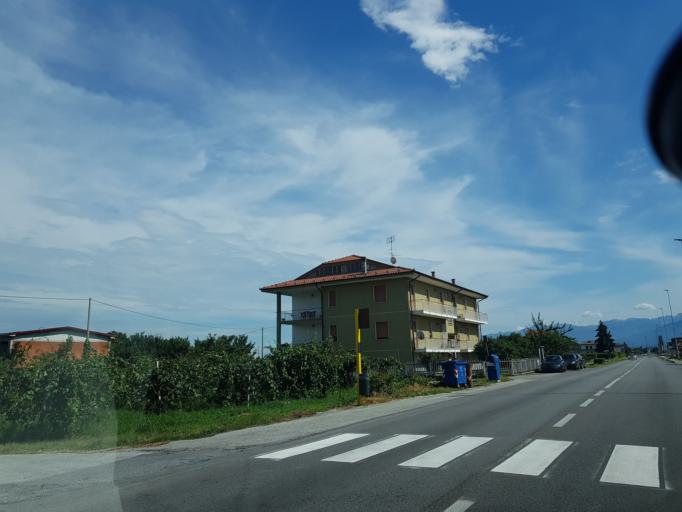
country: IT
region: Piedmont
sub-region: Provincia di Cuneo
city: Roata Rossi
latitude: 44.4770
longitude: 7.5073
